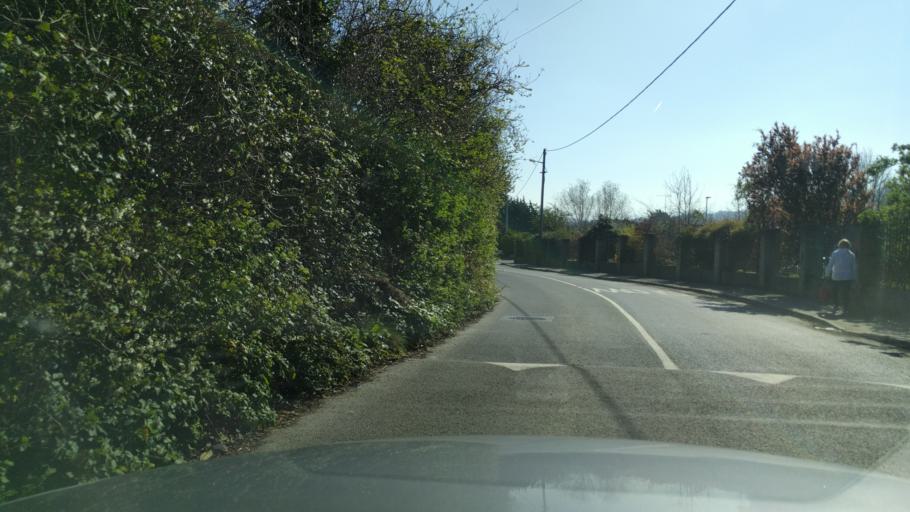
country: IE
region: Leinster
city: Firhouse
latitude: 53.2718
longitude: -6.3485
